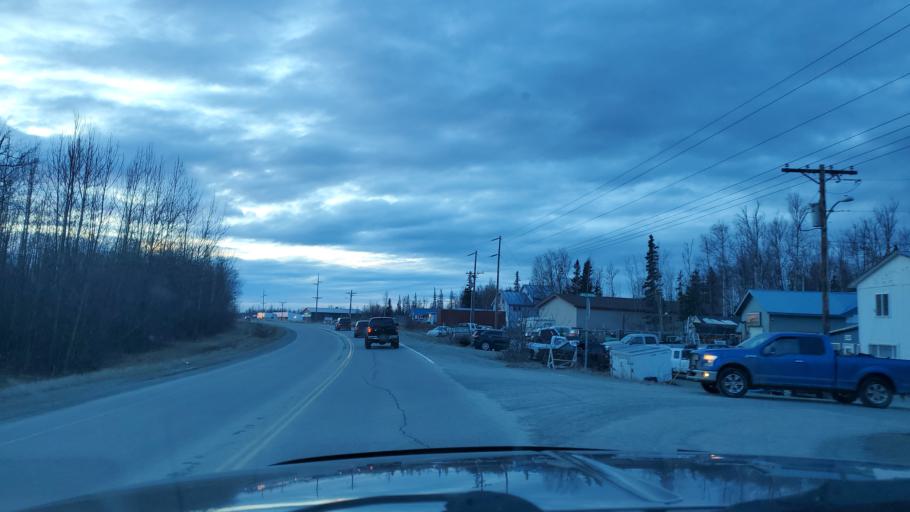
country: US
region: Alaska
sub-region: Matanuska-Susitna Borough
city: Wasilla
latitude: 61.5933
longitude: -149.3906
